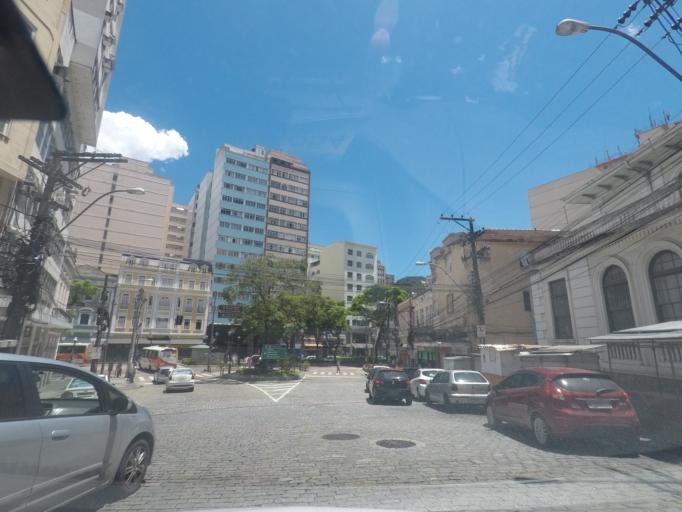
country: BR
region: Rio de Janeiro
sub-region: Petropolis
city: Petropolis
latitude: -22.5118
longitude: -43.1777
